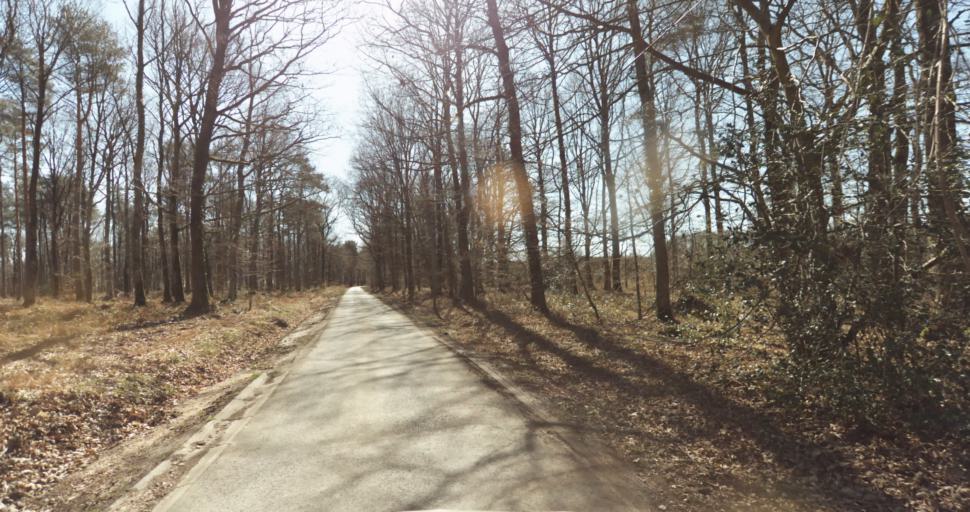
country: FR
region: Lower Normandy
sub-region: Departement du Calvados
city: Livarot
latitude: 48.9725
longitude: 0.0950
